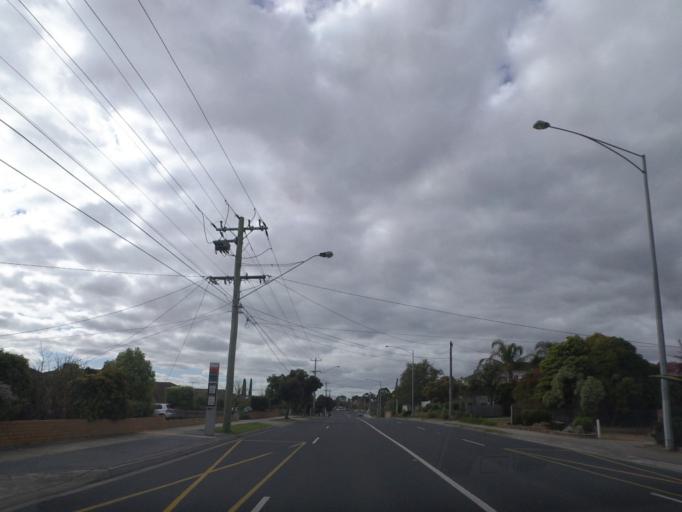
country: AU
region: Victoria
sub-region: Manningham
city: Templestowe Lower
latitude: -37.7767
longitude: 145.1138
